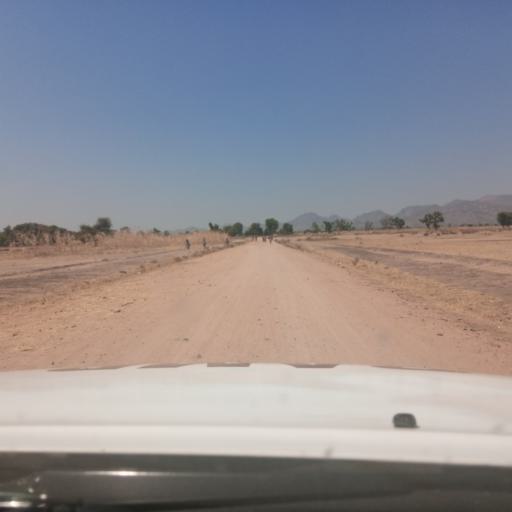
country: NG
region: Adamawa
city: Little Gombi
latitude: 9.7761
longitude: 12.5865
